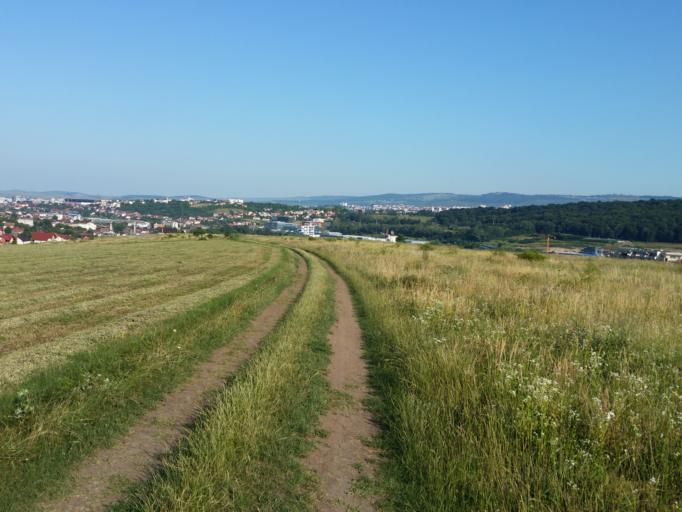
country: RO
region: Cluj
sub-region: Comuna Baciu
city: Baciu
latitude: 46.7888
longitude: 23.5391
